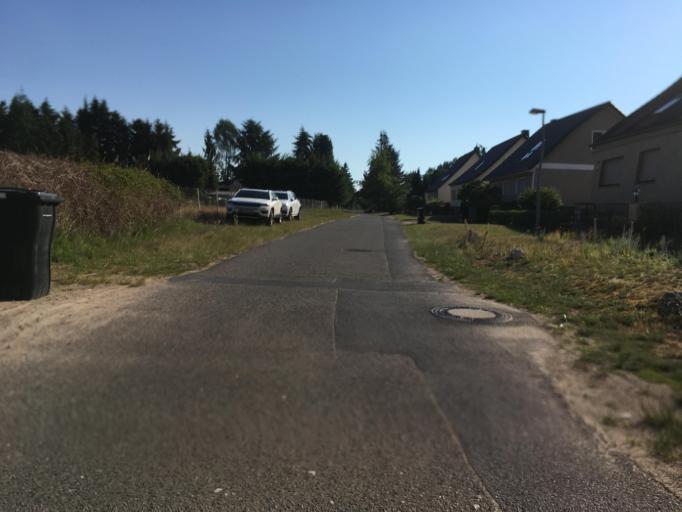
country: DE
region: Brandenburg
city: Marienwerder
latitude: 52.9111
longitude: 13.5431
